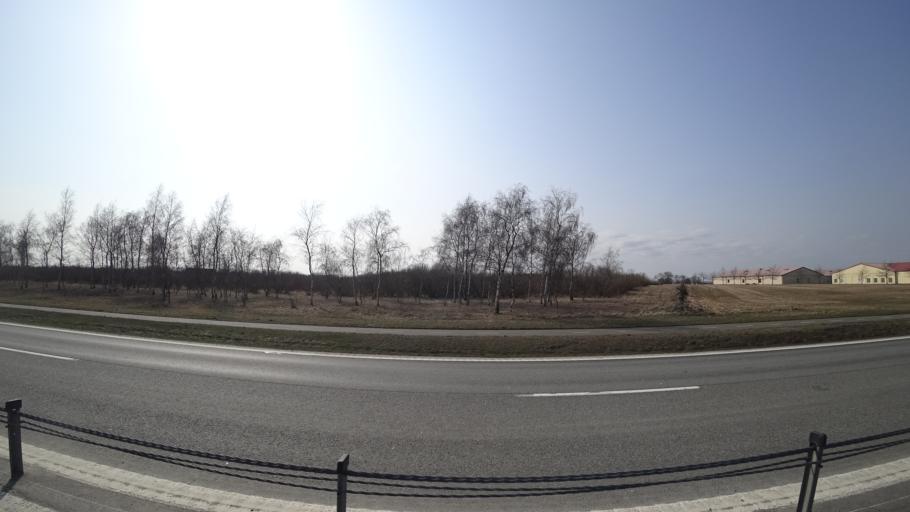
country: SE
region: Skane
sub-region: Kristianstads Kommun
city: Ahus
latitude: 55.9744
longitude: 14.2732
